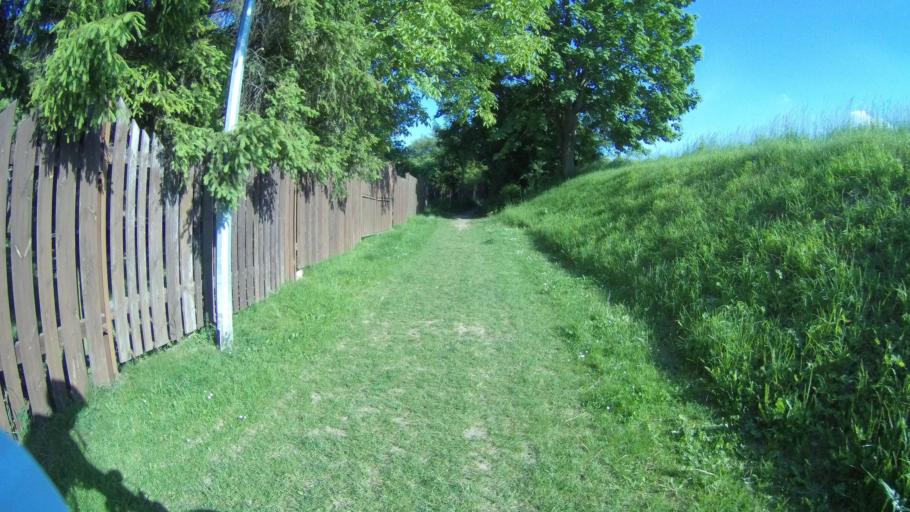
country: CZ
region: Central Bohemia
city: Klecany
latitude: 50.1672
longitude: 14.4298
